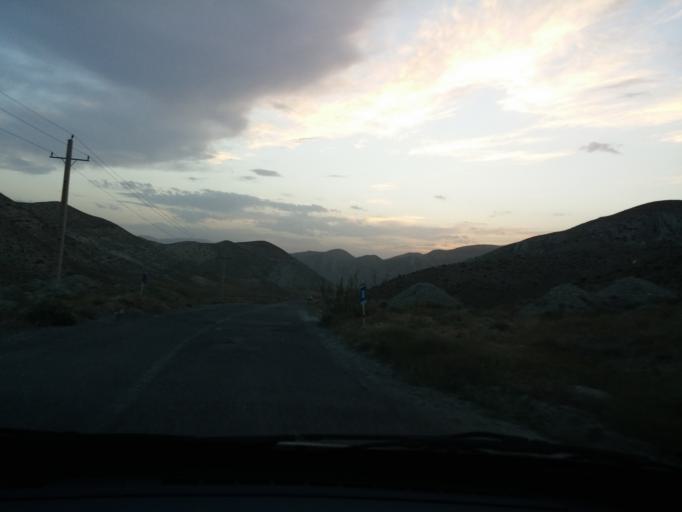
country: IR
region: Tehran
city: Damavand
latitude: 35.5456
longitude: 52.2769
